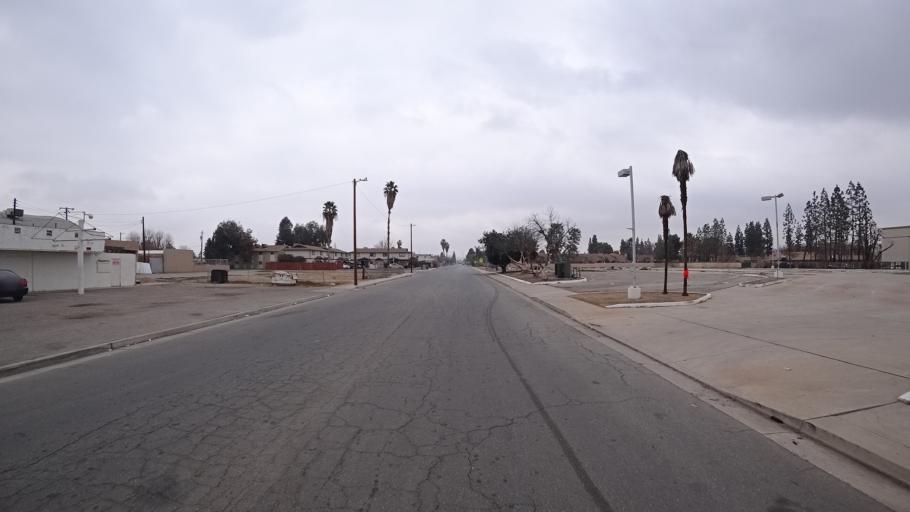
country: US
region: California
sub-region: Kern County
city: Bakersfield
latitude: 35.3908
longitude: -119.0129
